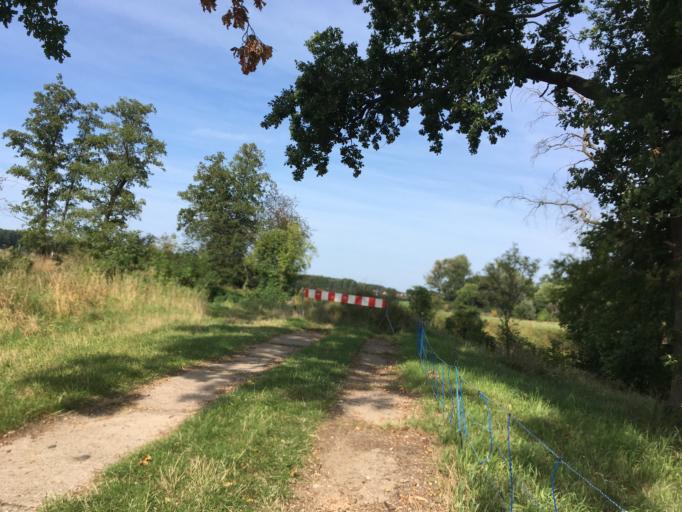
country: DE
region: Brandenburg
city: Guben
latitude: 52.0104
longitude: 14.7206
